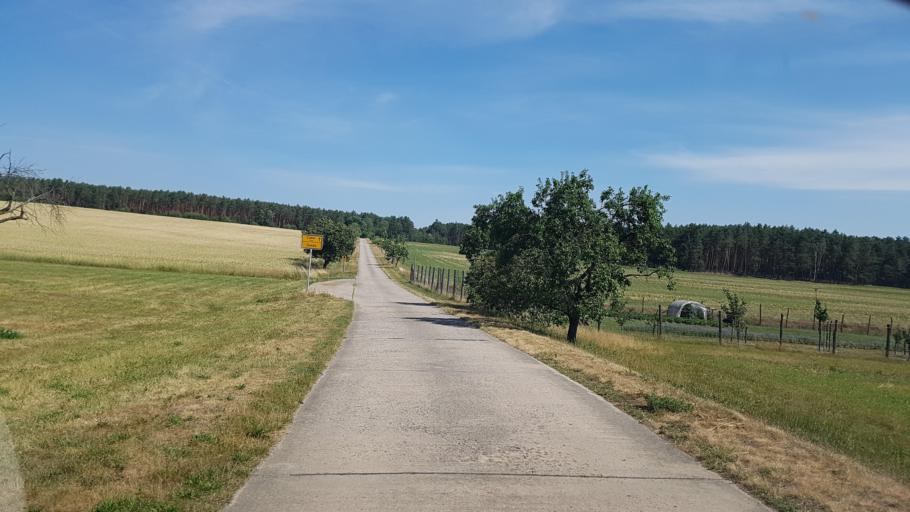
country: DE
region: Brandenburg
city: Bronkow
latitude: 51.6881
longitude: 13.9472
